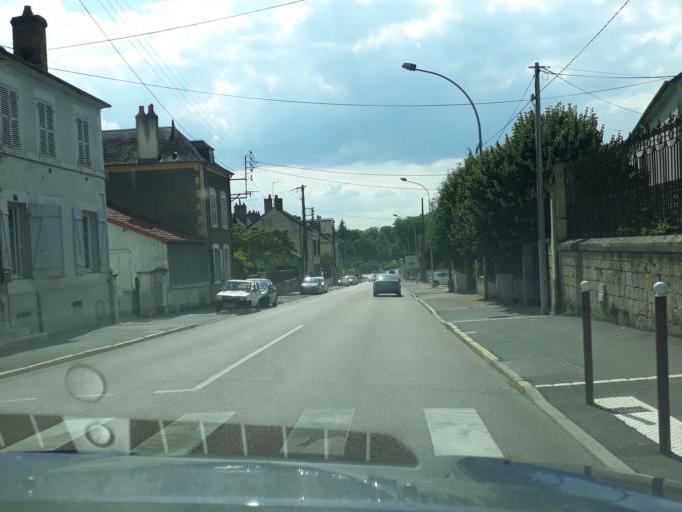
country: FR
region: Bourgogne
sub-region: Departement de la Nievre
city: Fourchambault
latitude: 47.0129
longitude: 3.0822
